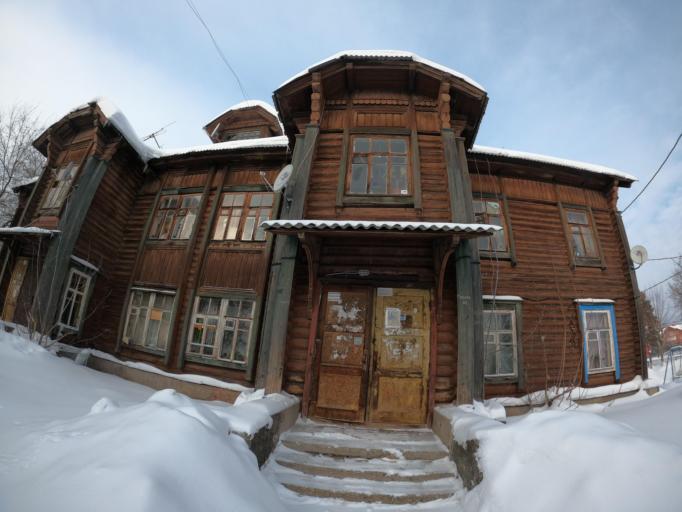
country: RU
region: Moskovskaya
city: Elektrogorsk
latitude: 55.8901
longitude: 38.7722
